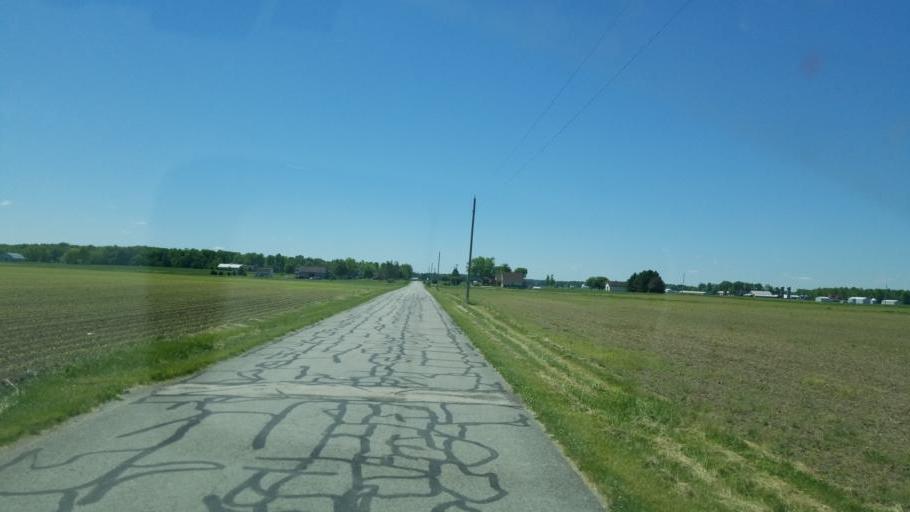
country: US
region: Ohio
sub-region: Shelby County
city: Fort Loramie
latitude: 40.3631
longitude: -84.3166
